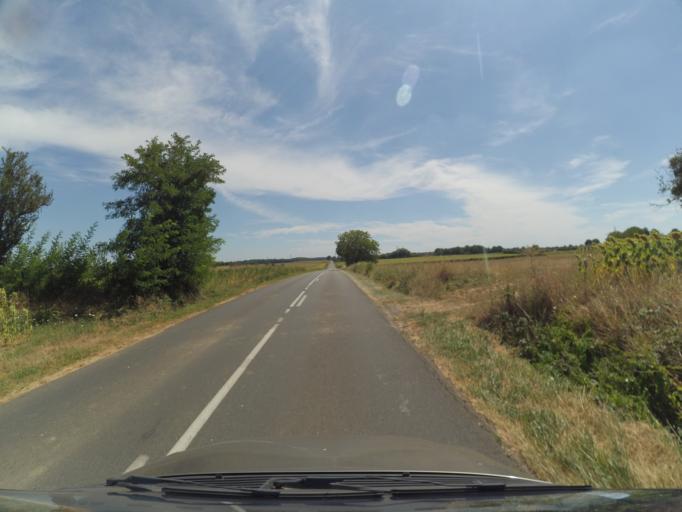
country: FR
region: Poitou-Charentes
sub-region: Departement de la Vienne
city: Usson-du-Poitou
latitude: 46.2968
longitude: 0.5054
